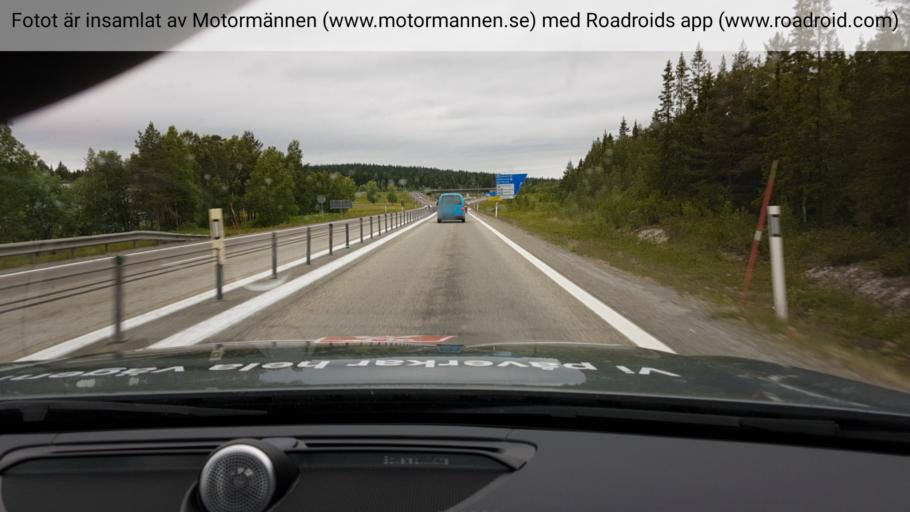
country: SE
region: Jaemtland
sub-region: OEstersunds Kommun
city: Ostersund
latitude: 63.1758
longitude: 14.6999
